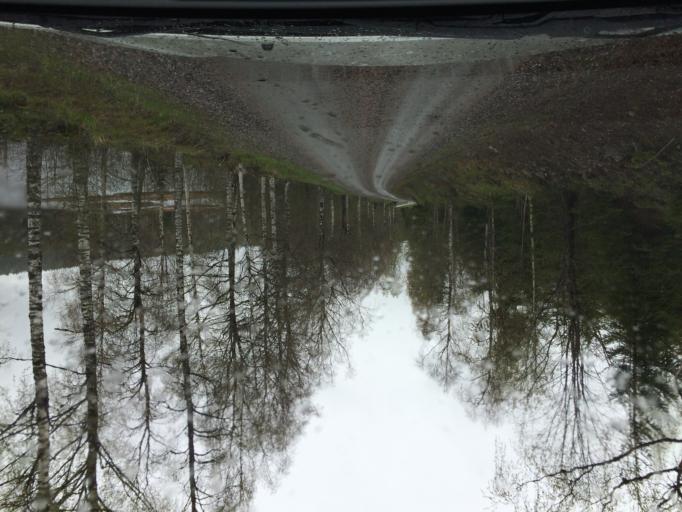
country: SE
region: Dalarna
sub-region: Ludvika Kommun
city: Abborrberget
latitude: 60.0247
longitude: 14.6362
